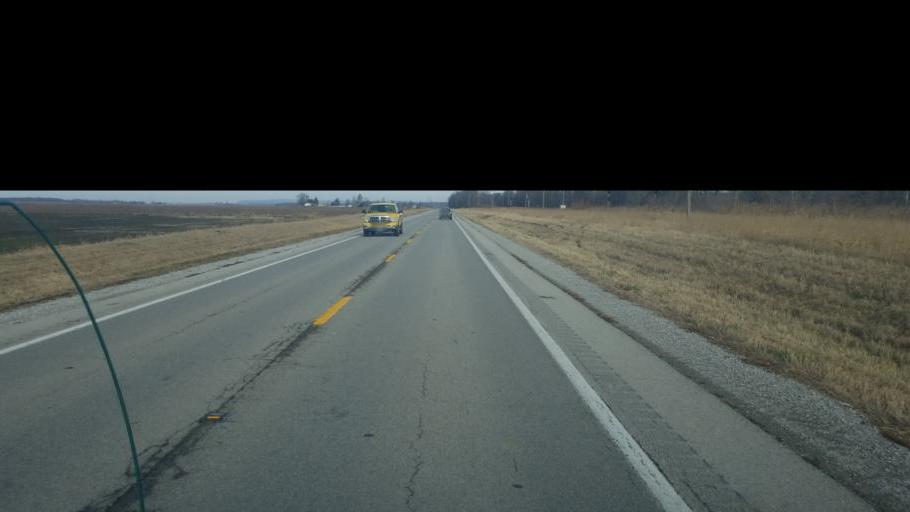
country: US
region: Illinois
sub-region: Union County
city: Jonesboro
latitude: 37.3875
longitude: -89.3890
